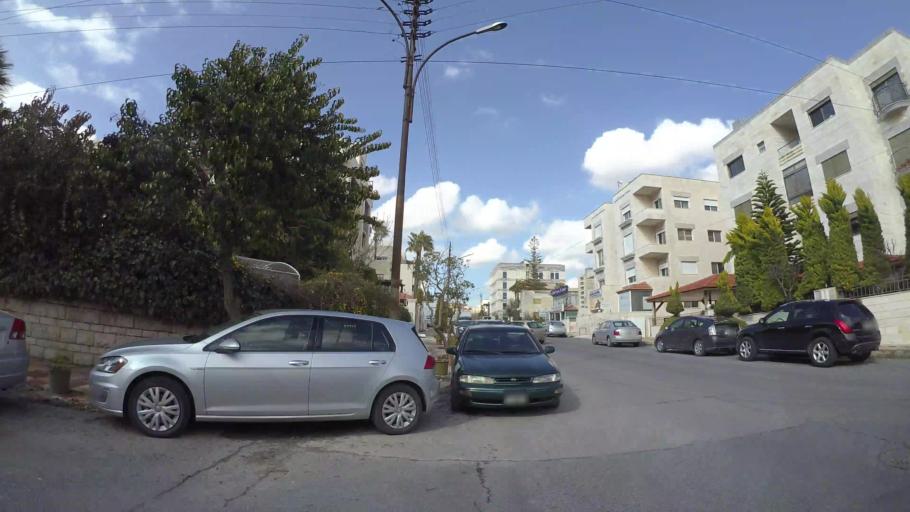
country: JO
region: Amman
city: Amman
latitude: 31.9690
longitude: 35.8917
